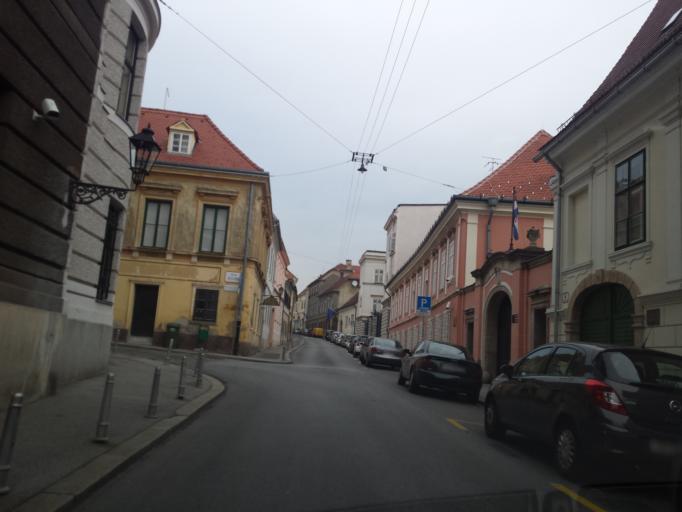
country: HR
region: Grad Zagreb
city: Zagreb
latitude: 45.8164
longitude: 15.9748
